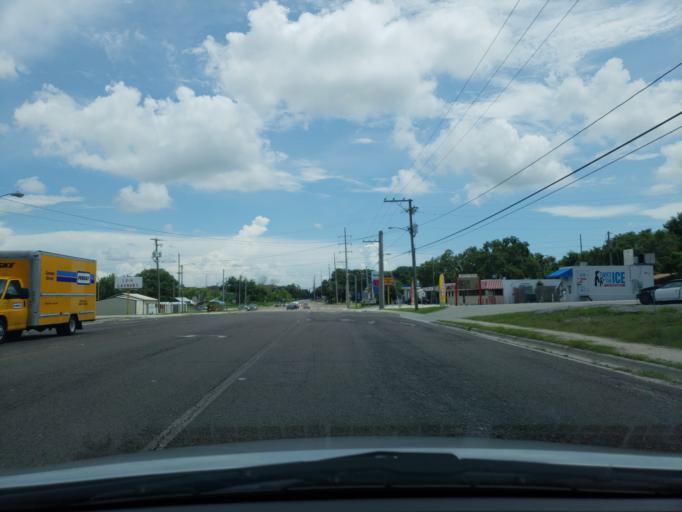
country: US
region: Florida
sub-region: Hillsborough County
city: East Lake-Orient Park
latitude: 27.9833
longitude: -82.3731
